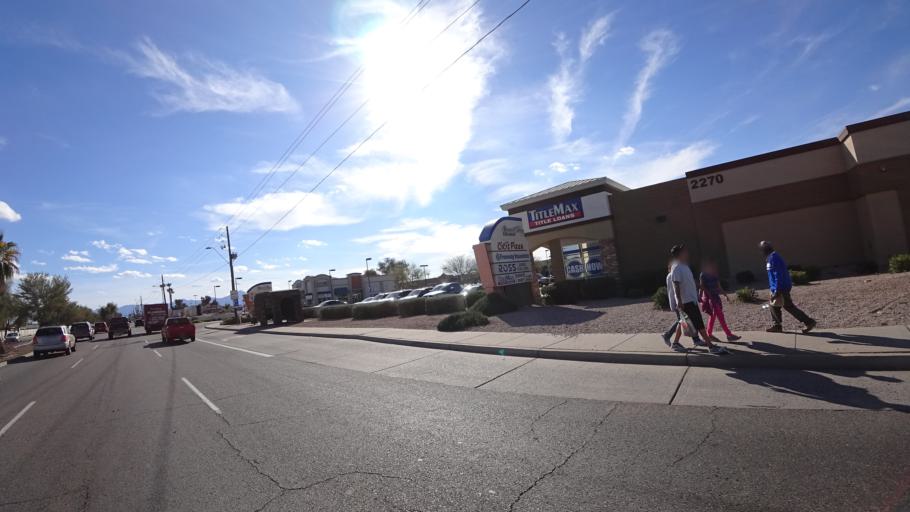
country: US
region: Arizona
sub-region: Maricopa County
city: Tolleson
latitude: 33.4727
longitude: -112.2209
